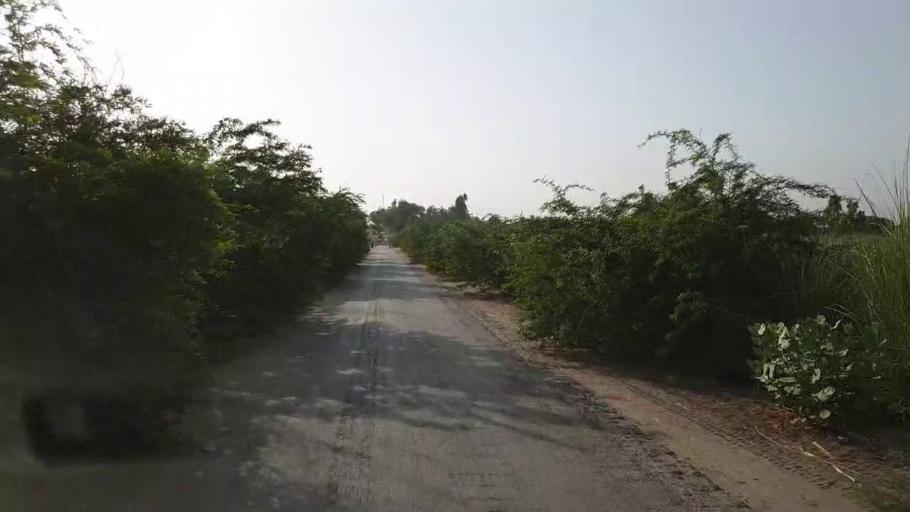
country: PK
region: Sindh
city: Jam Sahib
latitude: 26.4336
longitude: 68.8757
